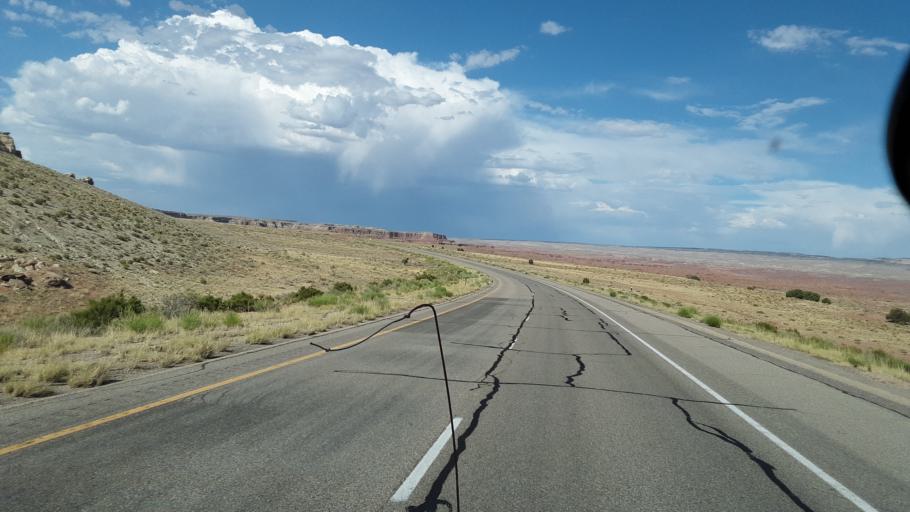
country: US
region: Utah
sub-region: Emery County
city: Ferron
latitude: 38.8314
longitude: -111.1090
